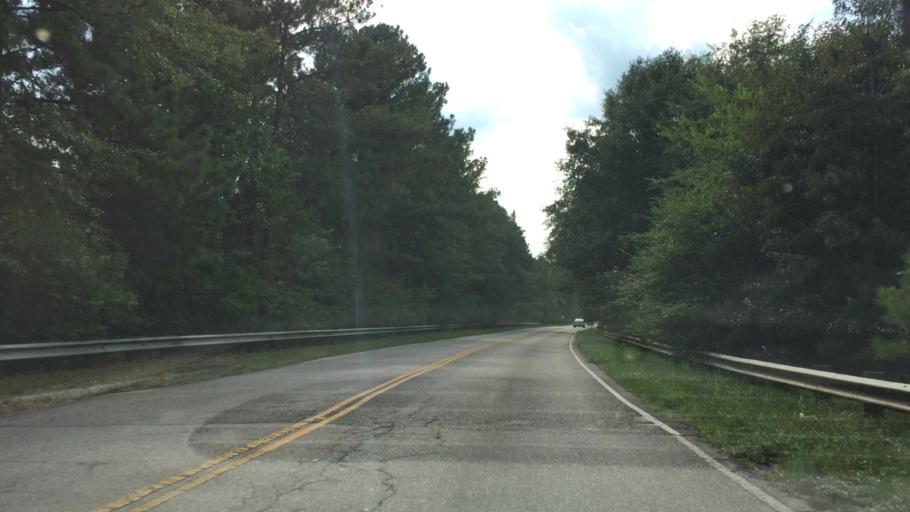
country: US
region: South Carolina
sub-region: Aiken County
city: Aiken
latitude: 33.5226
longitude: -81.7286
